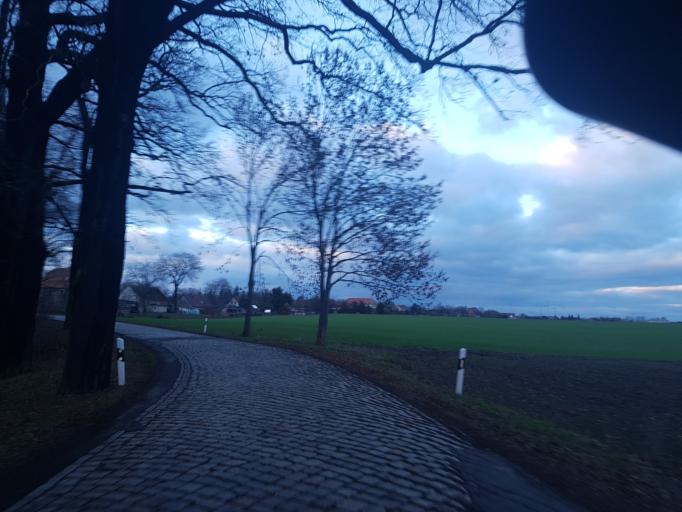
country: DE
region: Brandenburg
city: Muhlberg
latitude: 51.4668
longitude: 13.2055
